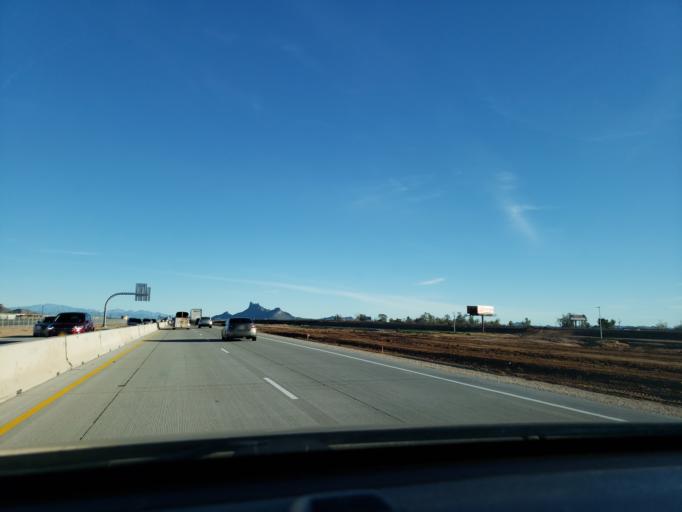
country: US
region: Arizona
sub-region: Pinal County
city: Eloy
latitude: 32.7179
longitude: -111.5034
